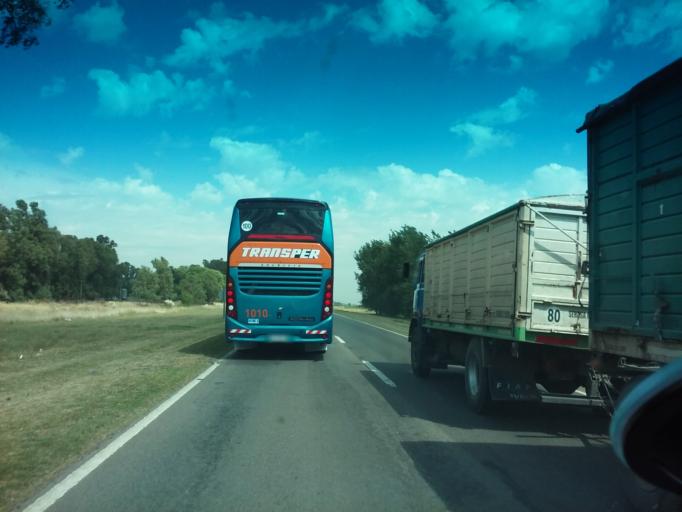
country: AR
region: Buenos Aires
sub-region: Partido de Carlos Casares
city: Carlos Casares
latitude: -35.6485
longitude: -61.3795
